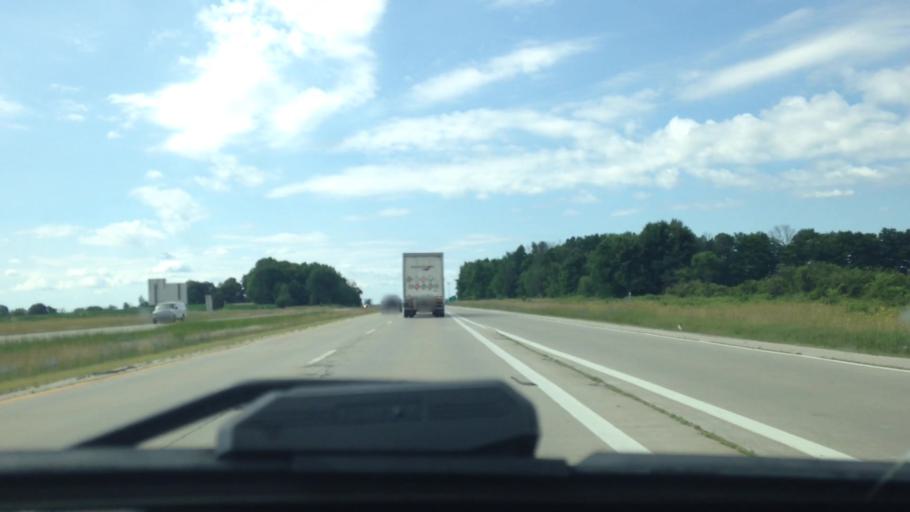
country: US
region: Wisconsin
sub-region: Washington County
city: Jackson
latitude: 43.3493
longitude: -88.1911
